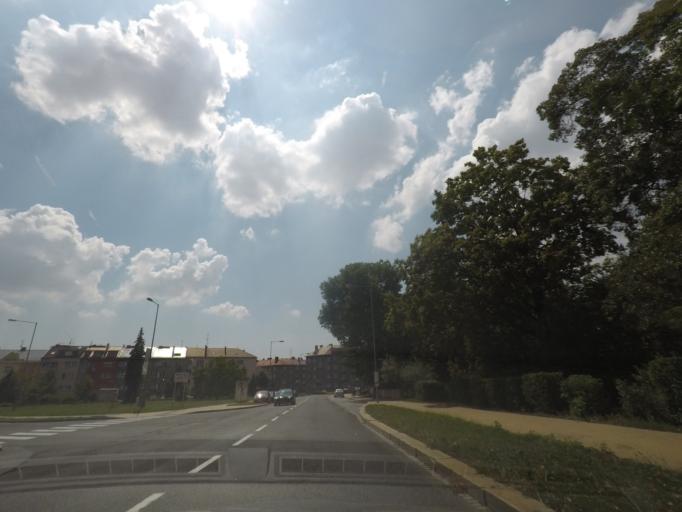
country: CZ
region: Olomoucky
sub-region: Okres Olomouc
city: Olomouc
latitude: 49.5865
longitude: 17.2548
